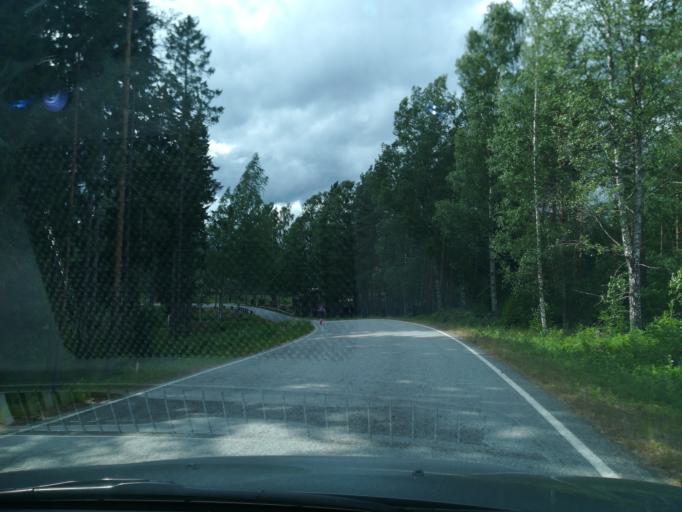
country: FI
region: South Karelia
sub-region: Lappeenranta
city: Savitaipale
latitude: 61.2615
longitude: 27.7143
